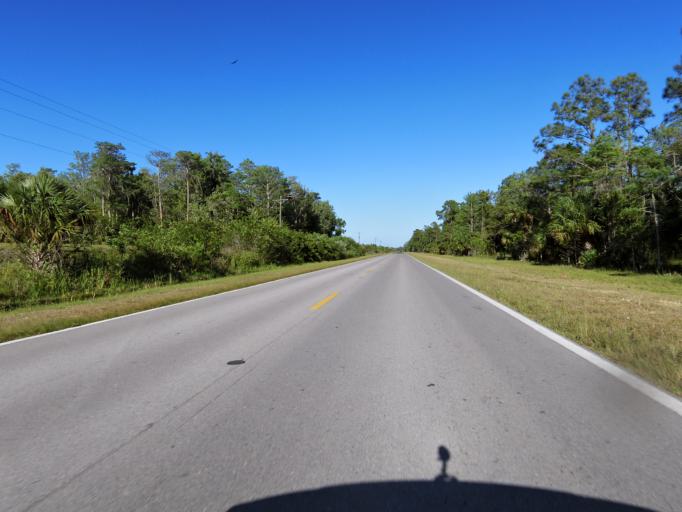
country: US
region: Florida
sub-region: Collier County
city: Immokalee
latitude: 26.2953
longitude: -81.3829
